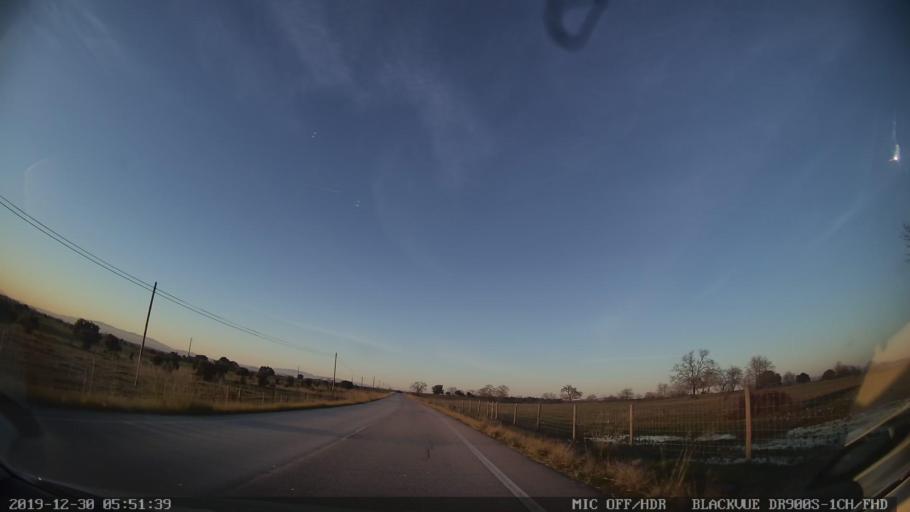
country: PT
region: Castelo Branco
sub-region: Idanha-A-Nova
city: Idanha-a-Nova
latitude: 39.9972
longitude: -7.2450
